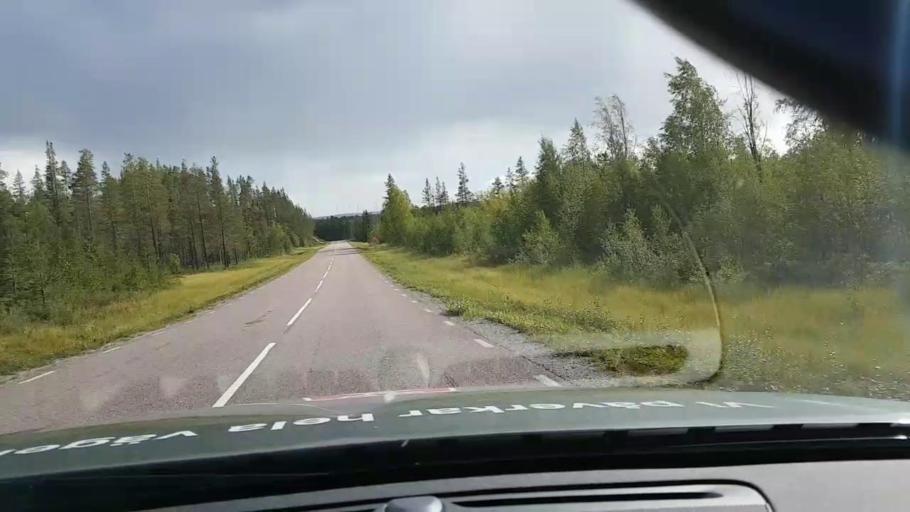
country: SE
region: Vaesterbotten
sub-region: Asele Kommun
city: Asele
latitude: 63.8708
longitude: 17.3573
